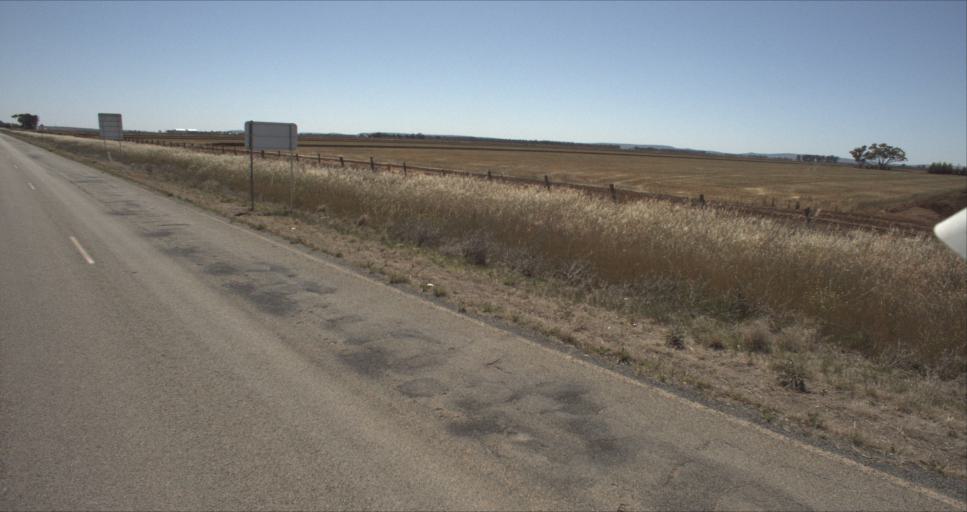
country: AU
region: New South Wales
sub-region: Leeton
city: Leeton
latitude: -34.5176
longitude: 146.2839
